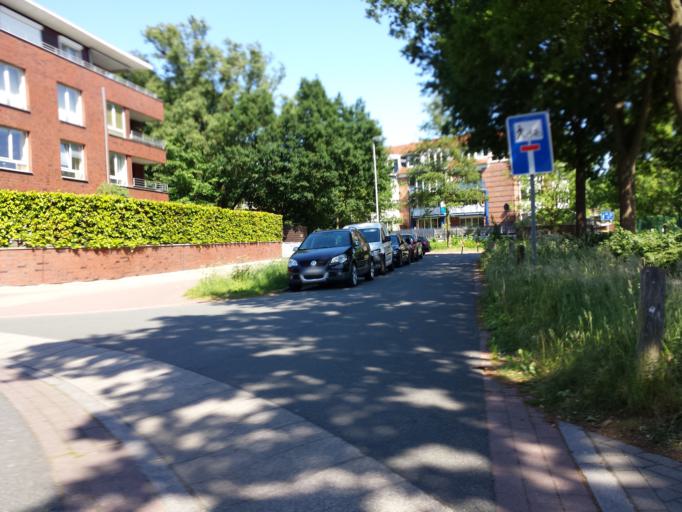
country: DE
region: Bremen
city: Bremen
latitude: 53.1028
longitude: 8.8628
